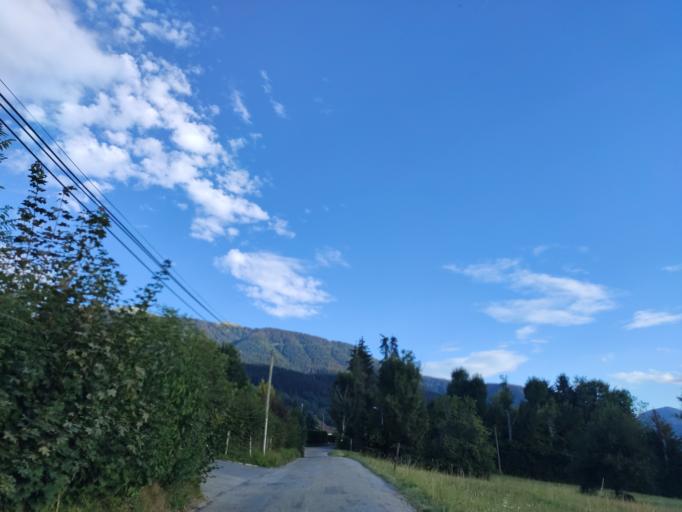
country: FR
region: Rhone-Alpes
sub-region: Departement de l'Isere
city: Revel
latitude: 45.1602
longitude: 5.8518
